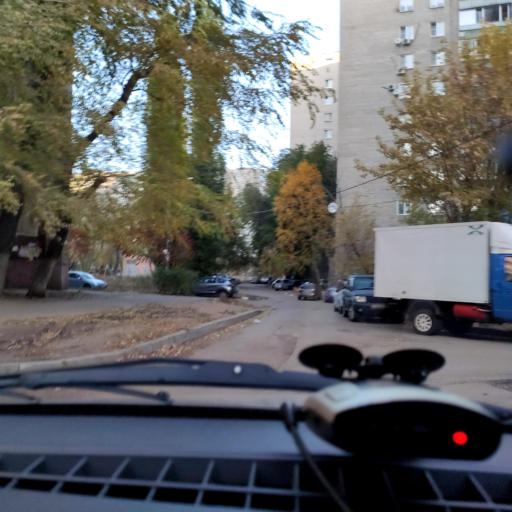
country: RU
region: Voronezj
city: Voronezh
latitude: 51.6851
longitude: 39.1980
